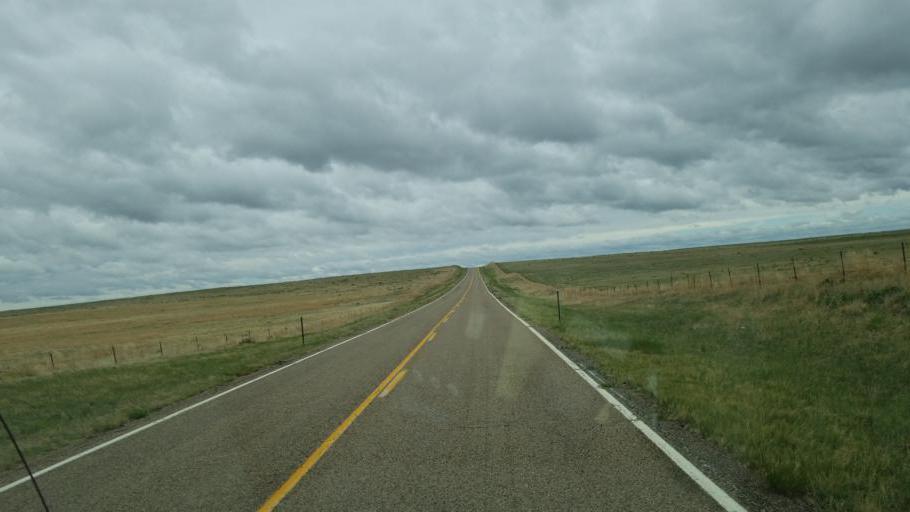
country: US
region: Colorado
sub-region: Lincoln County
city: Hugo
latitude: 38.8508
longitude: -103.5757
